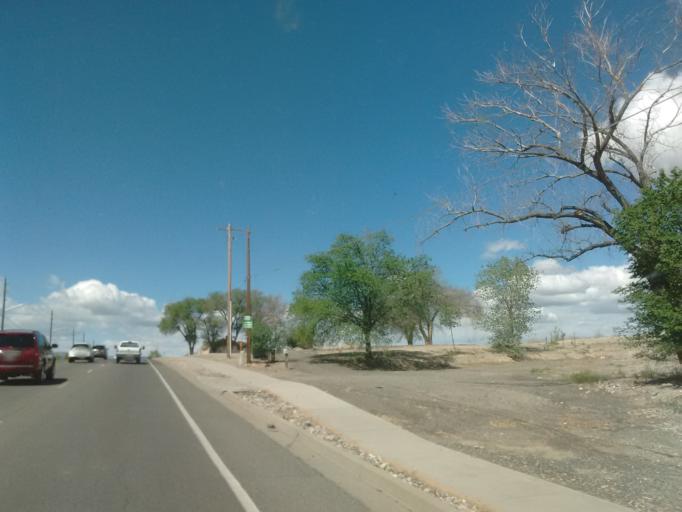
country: US
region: Colorado
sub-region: Mesa County
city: Fruitvale
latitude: 39.0919
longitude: -108.5238
